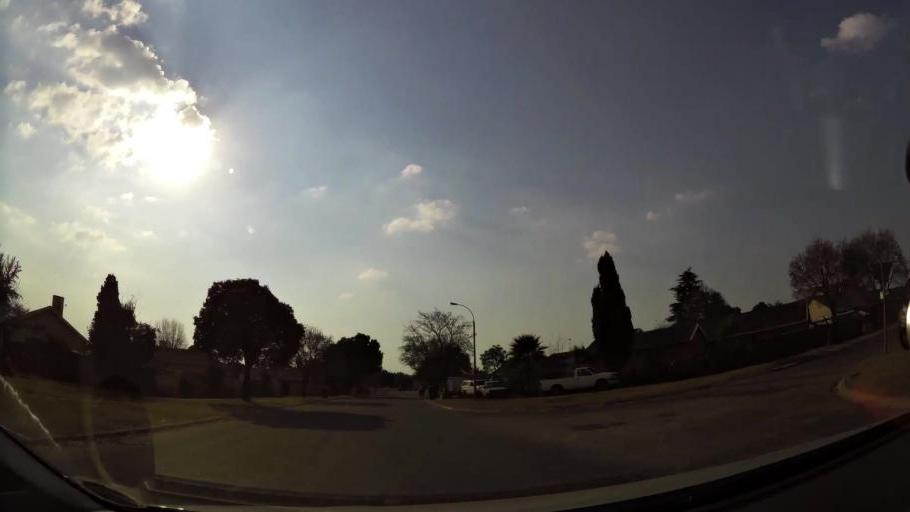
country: ZA
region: Gauteng
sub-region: City of Johannesburg Metropolitan Municipality
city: Modderfontein
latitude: -26.1027
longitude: 28.1931
